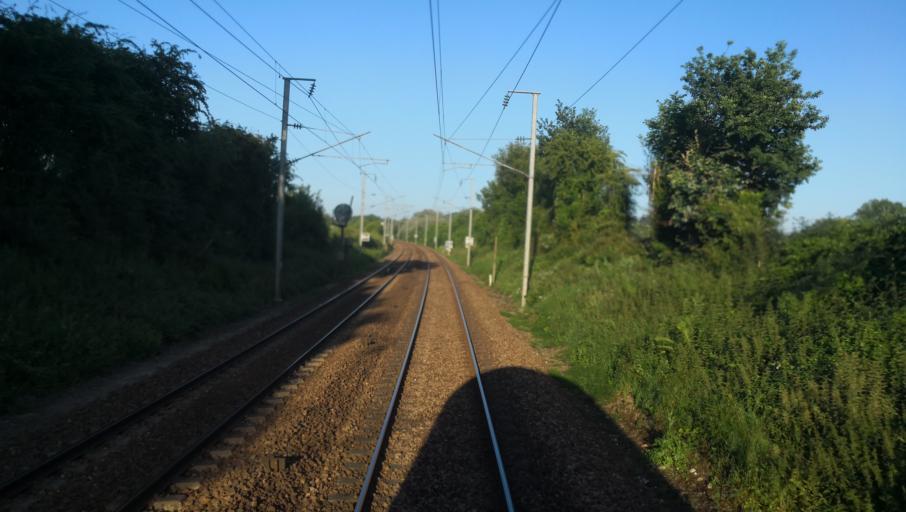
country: FR
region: Lower Normandy
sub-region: Departement du Calvados
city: Beuvillers
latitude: 49.1263
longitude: 0.2653
